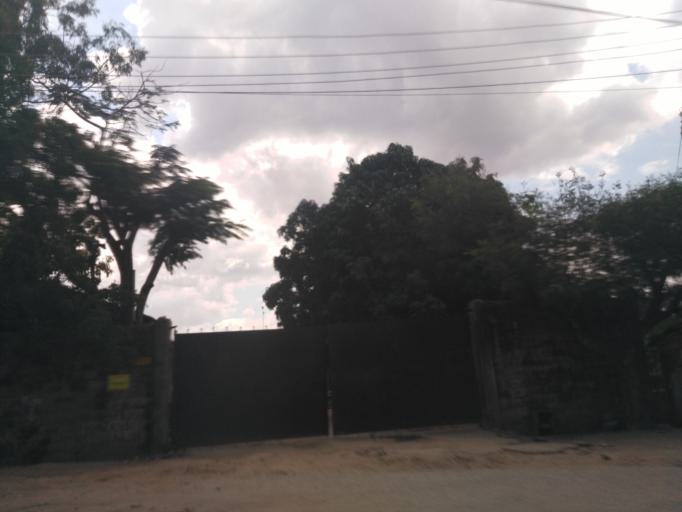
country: TZ
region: Dar es Salaam
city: Magomeni
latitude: -6.7671
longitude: 39.2473
